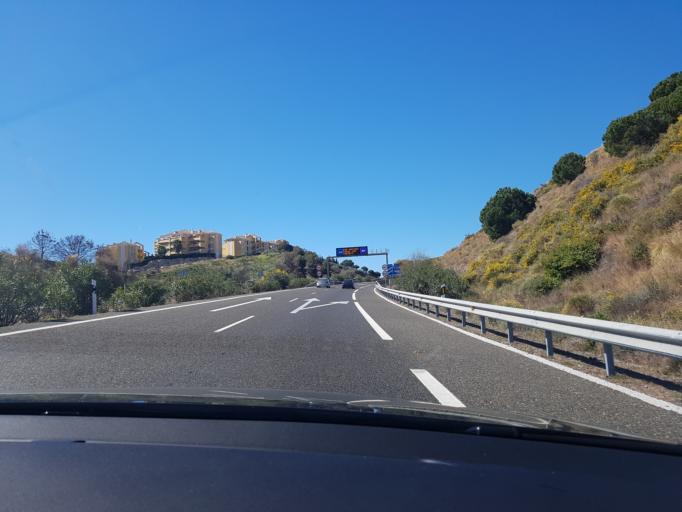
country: ES
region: Andalusia
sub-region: Provincia de Malaga
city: Fuengirola
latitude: 36.5075
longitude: -4.7087
